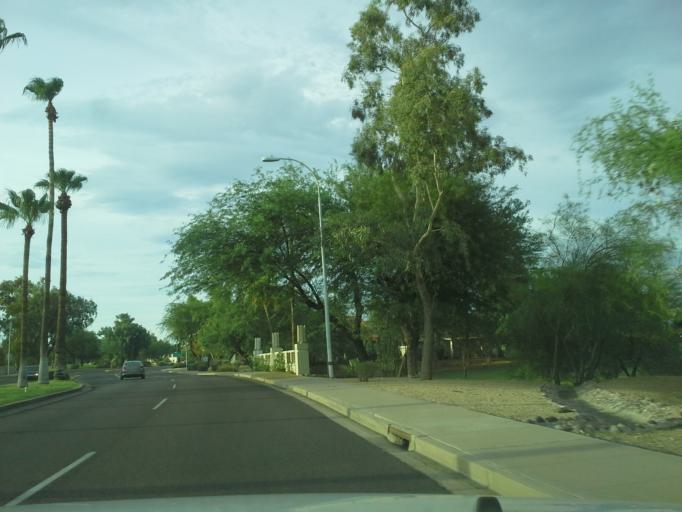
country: US
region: Arizona
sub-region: Maricopa County
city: Guadalupe
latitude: 33.3616
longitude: -111.9750
